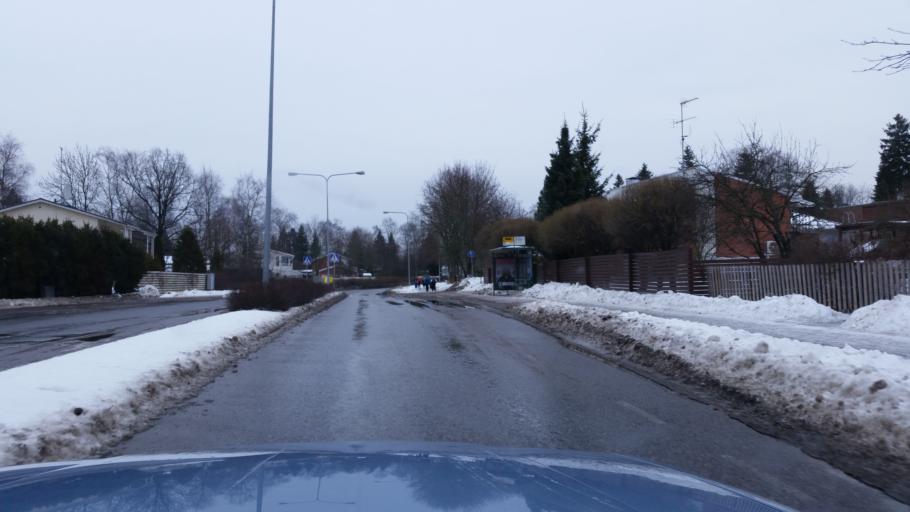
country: FI
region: Uusimaa
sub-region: Helsinki
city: Vantaa
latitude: 60.2713
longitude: 25.0458
